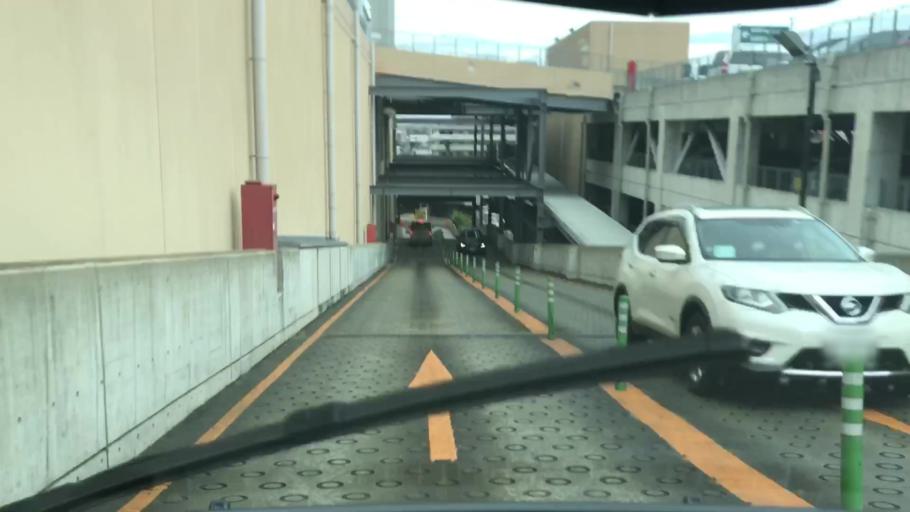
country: JP
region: Hyogo
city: Nishinomiya-hama
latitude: 34.7438
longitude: 135.3577
